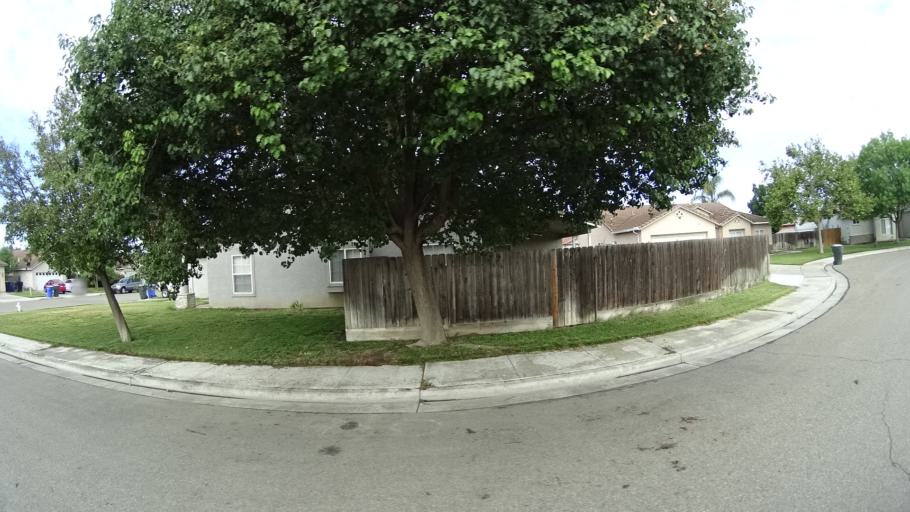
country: US
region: California
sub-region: Kings County
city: Hanford
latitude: 36.3618
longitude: -119.6298
